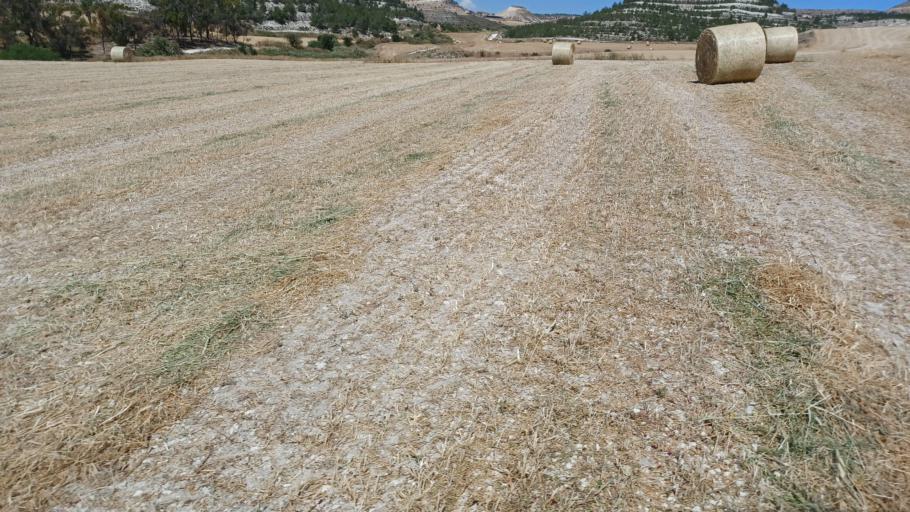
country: CY
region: Lefkosia
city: Lympia
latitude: 34.9926
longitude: 33.5300
